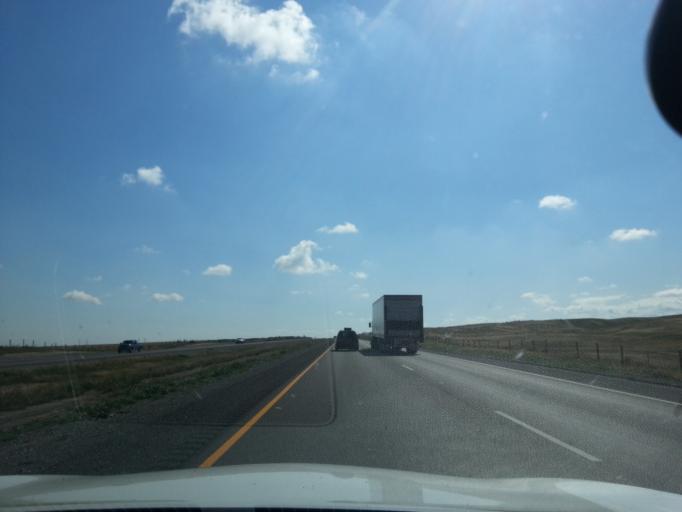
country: US
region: California
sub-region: Fresno County
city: Mendota
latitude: 36.5398
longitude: -120.5001
